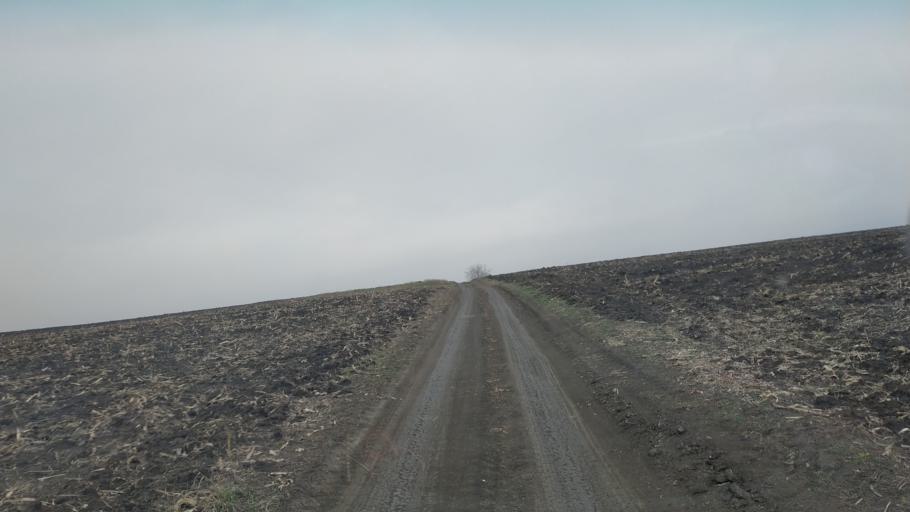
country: MD
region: Chisinau
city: Singera
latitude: 46.8281
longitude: 29.0012
